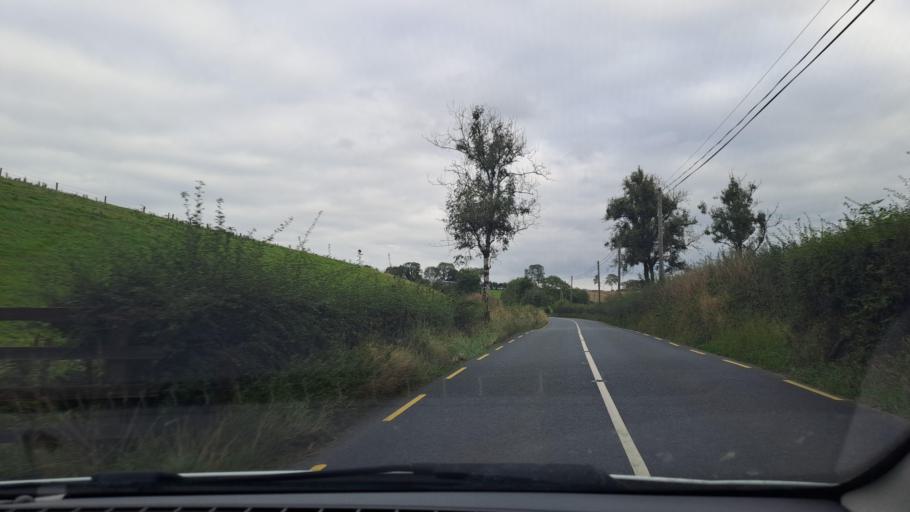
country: IE
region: Ulster
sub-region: An Cabhan
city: Kingscourt
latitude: 54.0000
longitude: -6.8642
